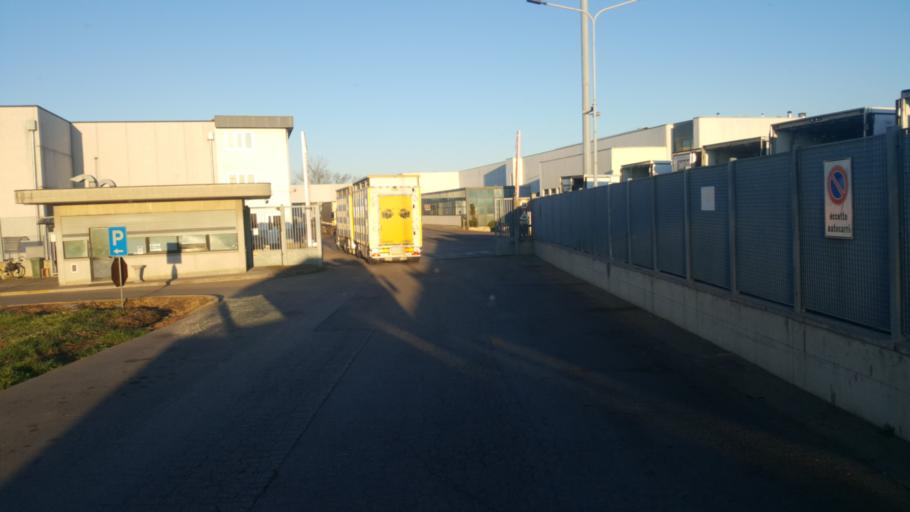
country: IT
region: Emilia-Romagna
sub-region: Provincia di Modena
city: Ca' di Sola
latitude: 44.5362
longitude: 10.9678
